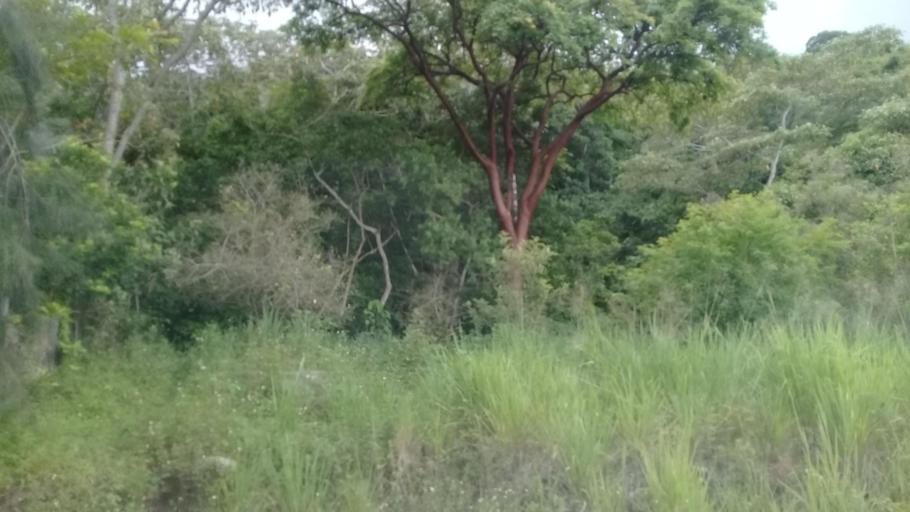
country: MX
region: Veracruz
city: El Castillo
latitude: 19.5650
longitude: -96.8477
